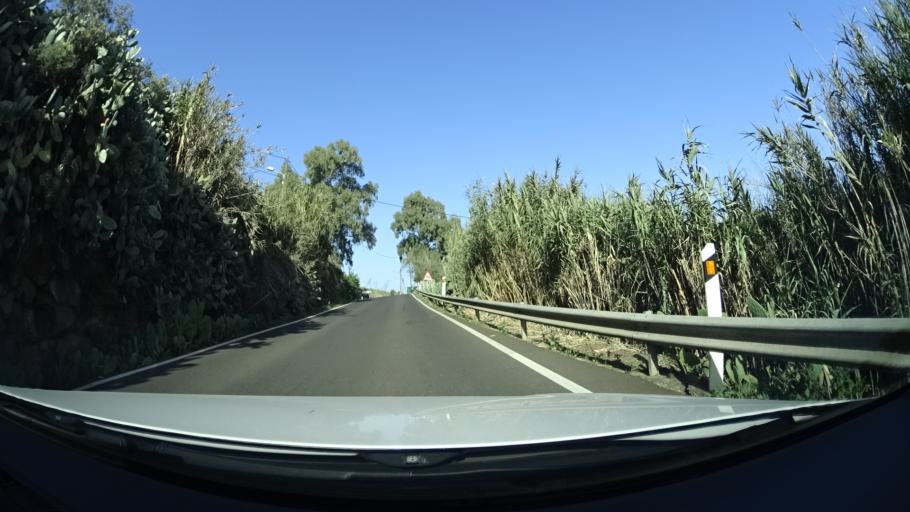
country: ES
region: Canary Islands
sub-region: Provincia de Las Palmas
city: Vega de San Mateo
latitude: 28.0183
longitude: -15.5412
